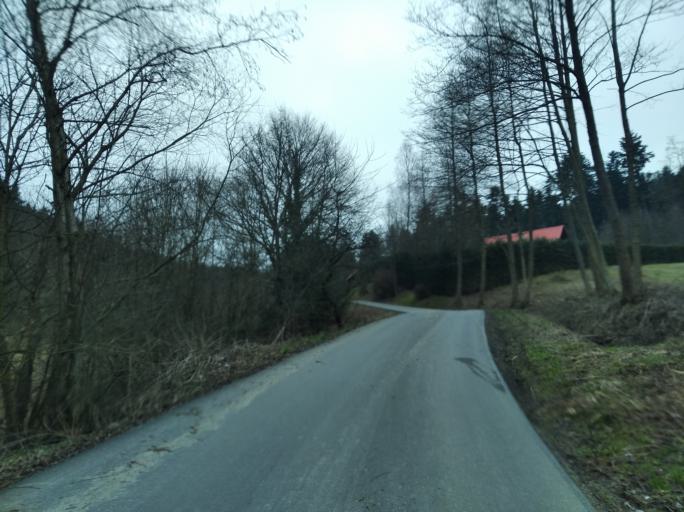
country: PL
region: Subcarpathian Voivodeship
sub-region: Powiat strzyzowski
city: Strzyzow
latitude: 49.8580
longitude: 21.8318
